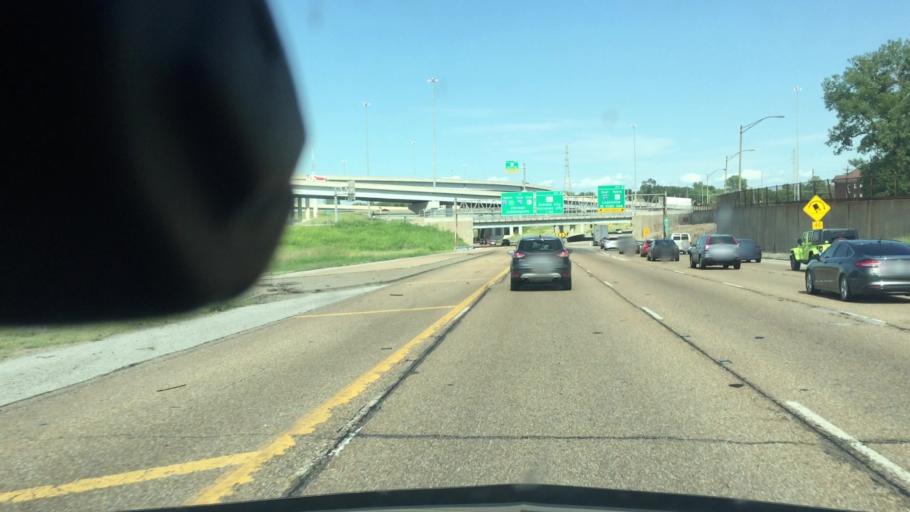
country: US
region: Illinois
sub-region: Saint Clair County
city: East Saint Louis
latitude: 38.6324
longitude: -90.1481
